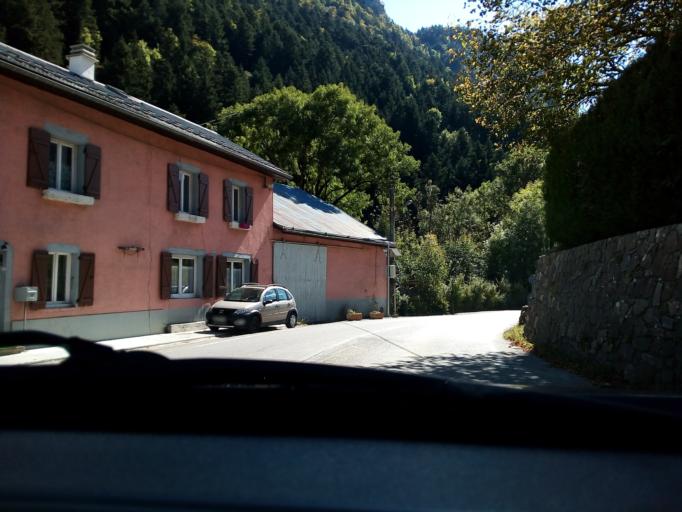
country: FR
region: Rhone-Alpes
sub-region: Departement de l'Isere
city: Sassenage
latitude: 45.1759
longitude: 5.6181
